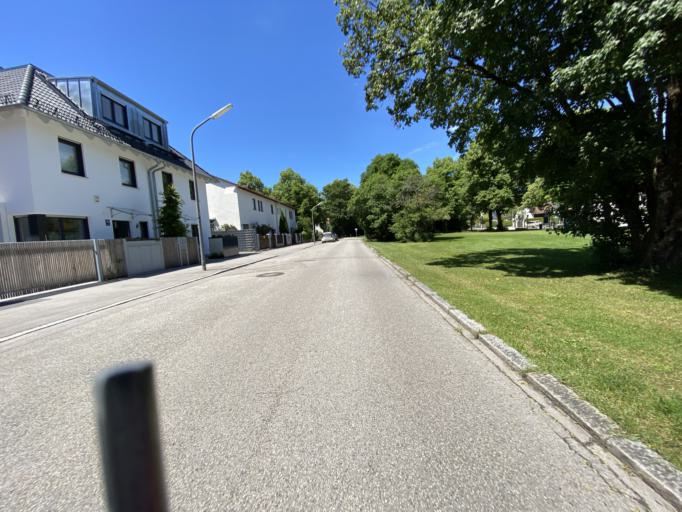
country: DE
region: Bavaria
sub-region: Upper Bavaria
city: Neubiberg
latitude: 48.1193
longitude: 11.6506
